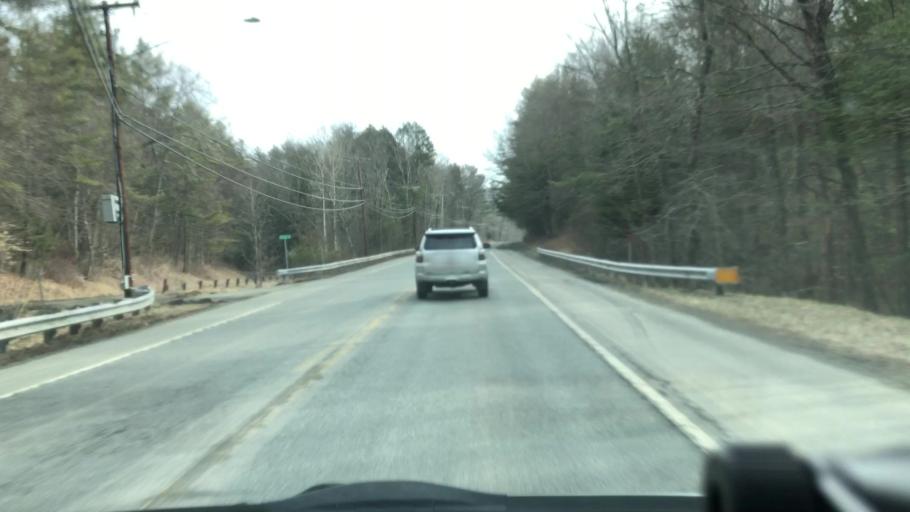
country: US
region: Massachusetts
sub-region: Franklin County
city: Shelburne
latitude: 42.5944
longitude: -72.6793
